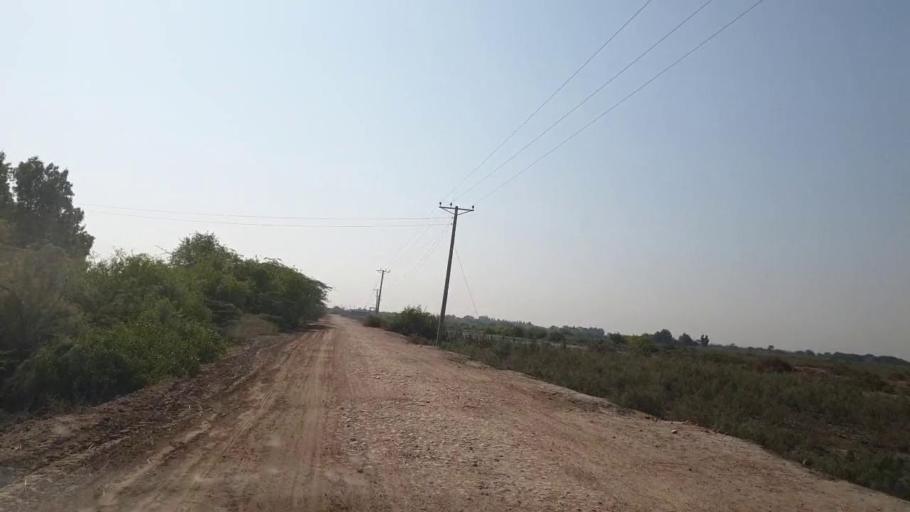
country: PK
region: Sindh
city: Thatta
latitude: 24.7285
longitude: 67.7940
